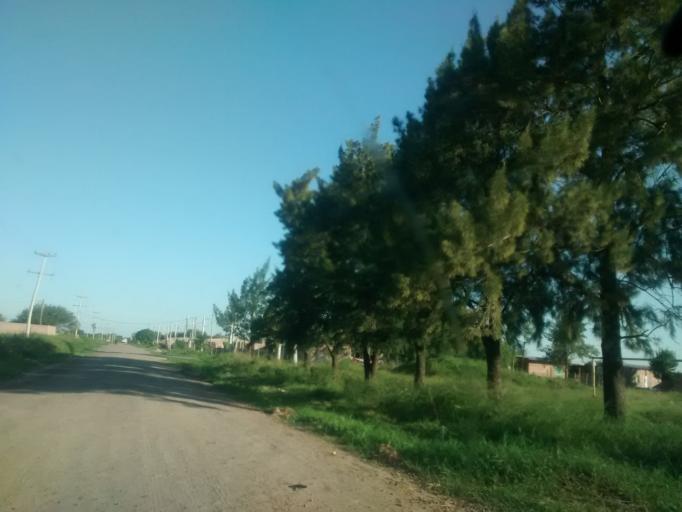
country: AR
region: Chaco
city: Fontana
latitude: -27.4607
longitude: -59.0332
